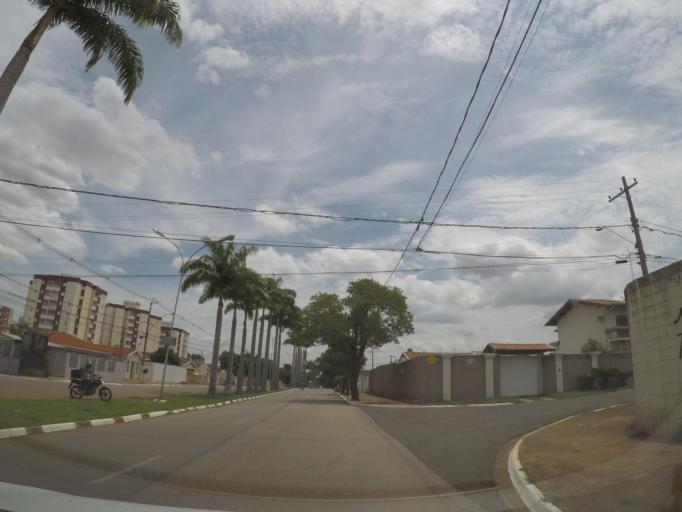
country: BR
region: Sao Paulo
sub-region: Sumare
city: Sumare
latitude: -22.8335
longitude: -47.2659
